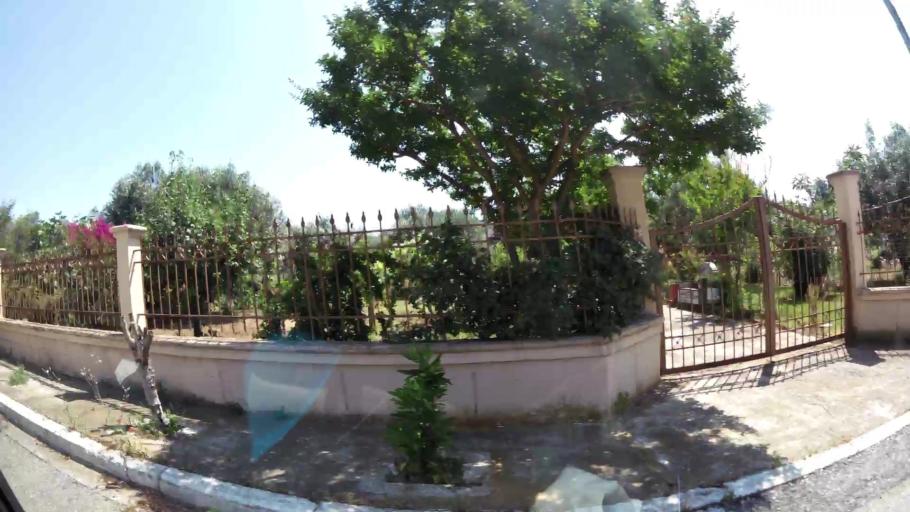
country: GR
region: Central Macedonia
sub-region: Nomos Thessalonikis
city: Agia Triada
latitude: 40.4987
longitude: 22.8365
